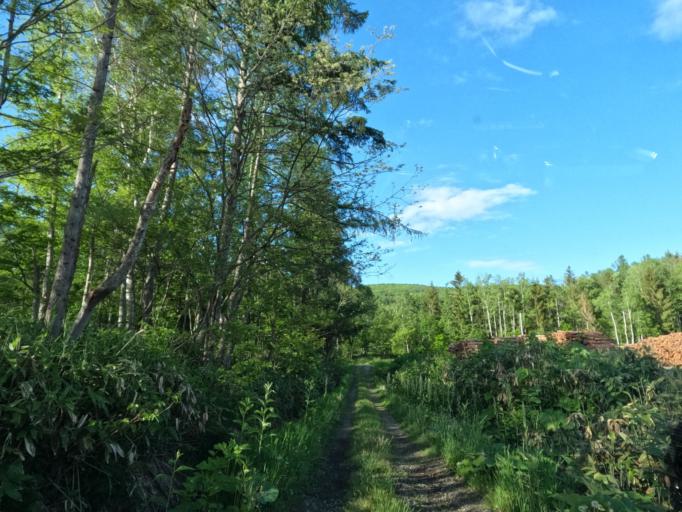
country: JP
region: Hokkaido
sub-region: Asahikawa-shi
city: Asahikawa
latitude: 43.9221
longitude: 142.4967
